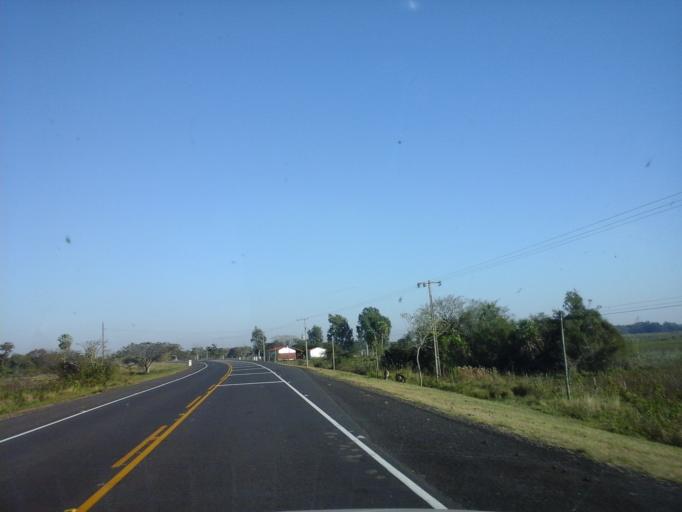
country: PY
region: Neembucu
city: Pilar
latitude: -26.8654
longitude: -58.1316
